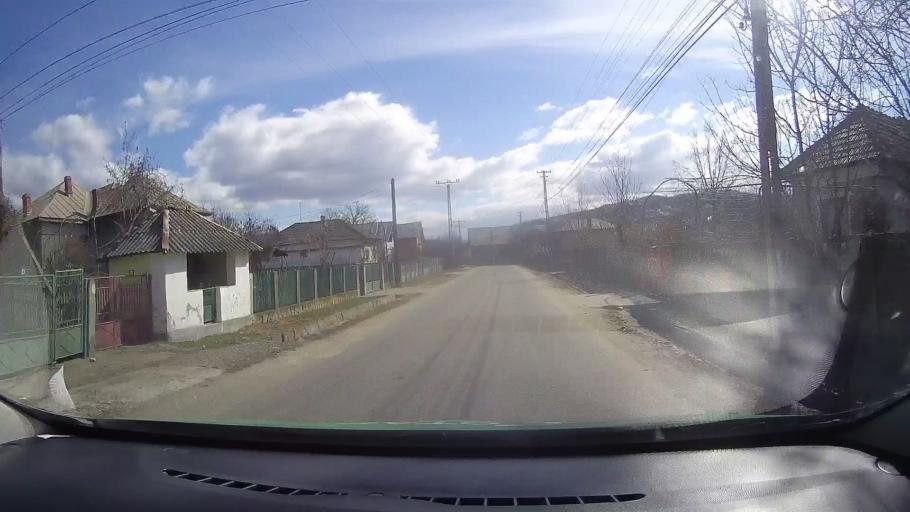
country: RO
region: Dambovita
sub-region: Comuna Branesti
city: Branesti
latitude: 45.0320
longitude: 25.4164
